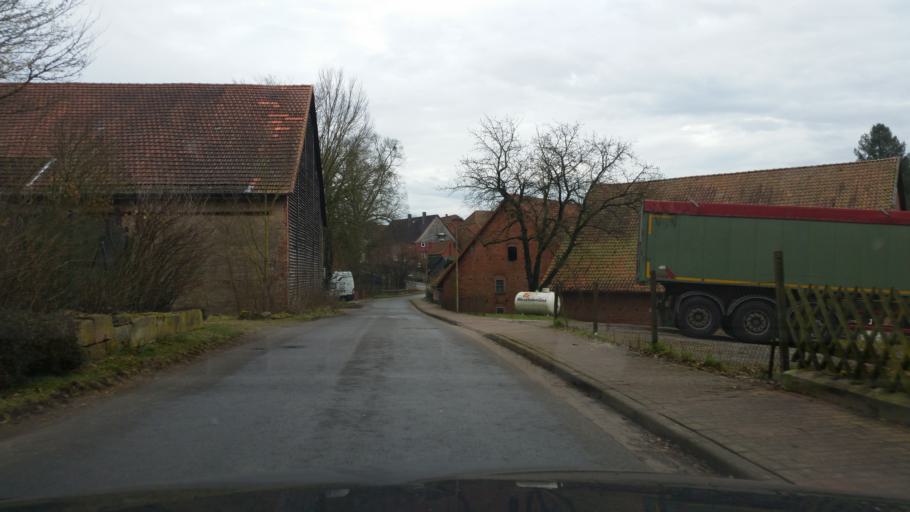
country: DE
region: Lower Saxony
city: Hameln
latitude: 52.1605
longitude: 9.3554
